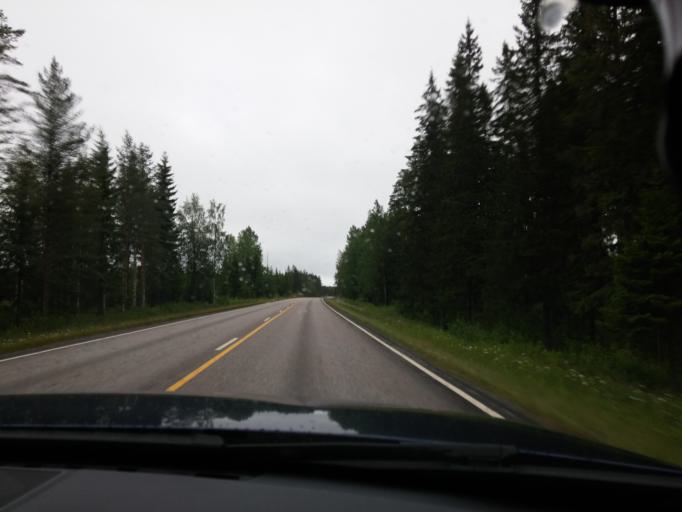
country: FI
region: Pirkanmaa
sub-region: Ylae-Pirkanmaa
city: Vilppula
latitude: 61.9167
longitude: 24.5326
